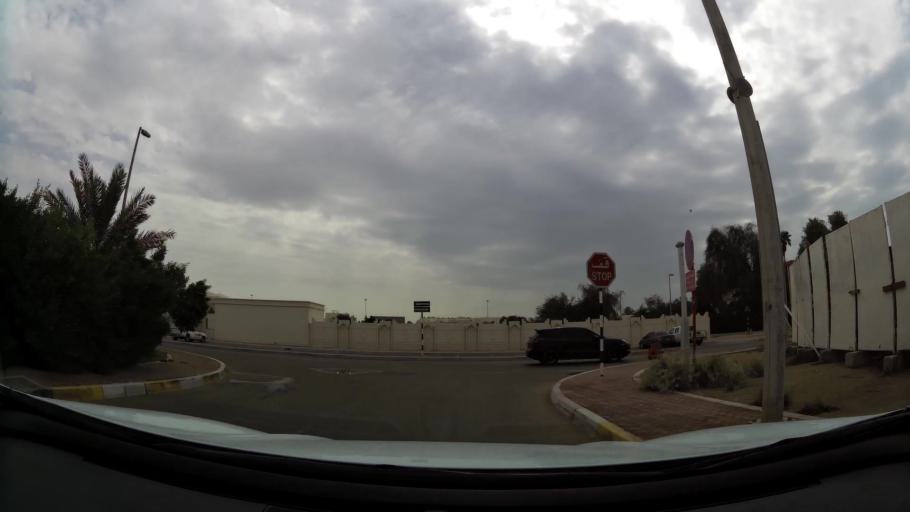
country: AE
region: Abu Dhabi
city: Abu Dhabi
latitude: 24.4267
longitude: 54.4144
